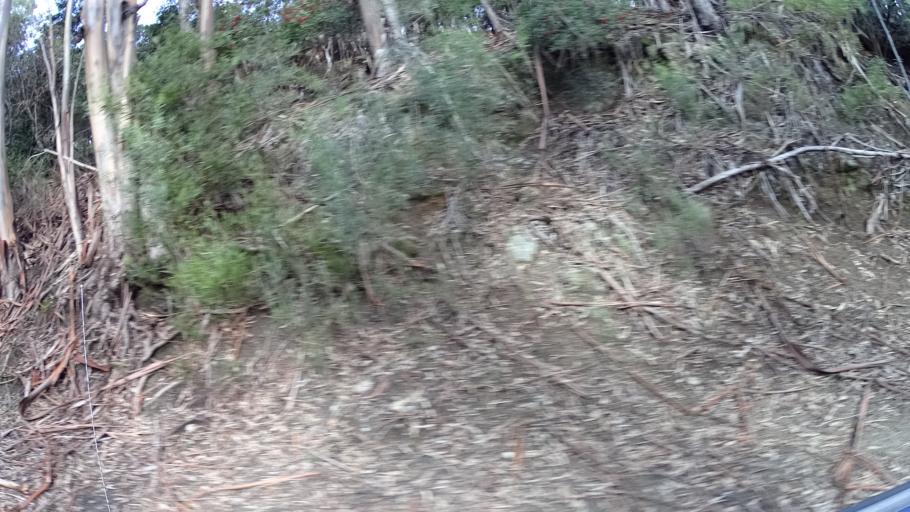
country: US
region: California
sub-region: San Mateo County
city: Hillsborough
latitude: 37.5534
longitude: -122.3621
